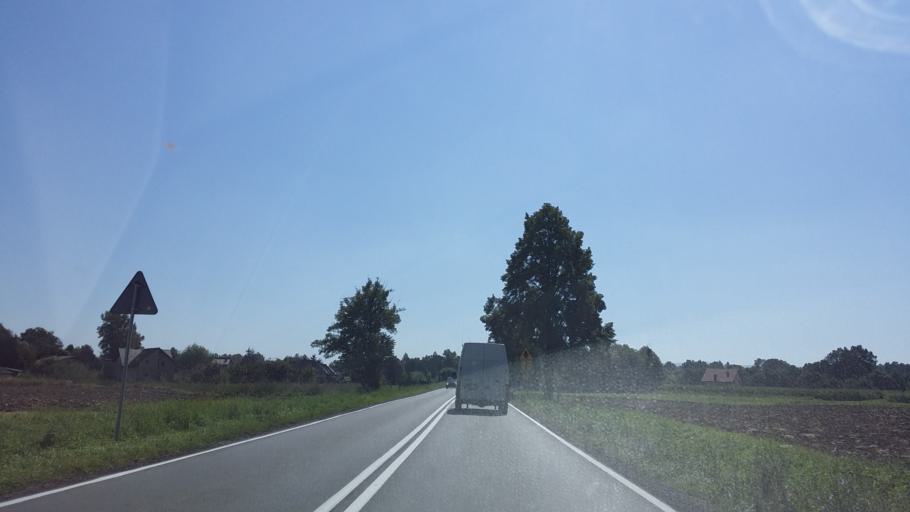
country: PL
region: Lesser Poland Voivodeship
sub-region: Powiat oswiecimski
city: Zator
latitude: 49.9652
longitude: 19.4410
